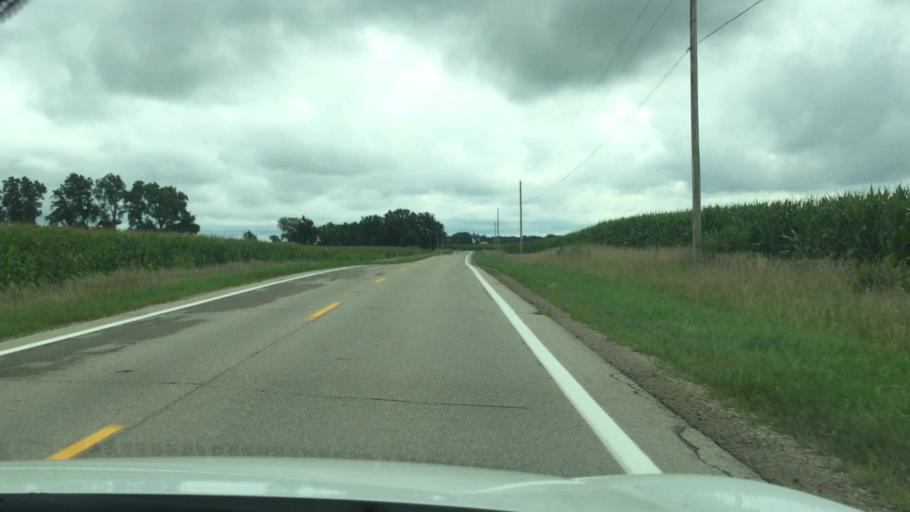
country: US
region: Ohio
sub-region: Champaign County
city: North Lewisburg
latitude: 40.1544
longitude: -83.5282
